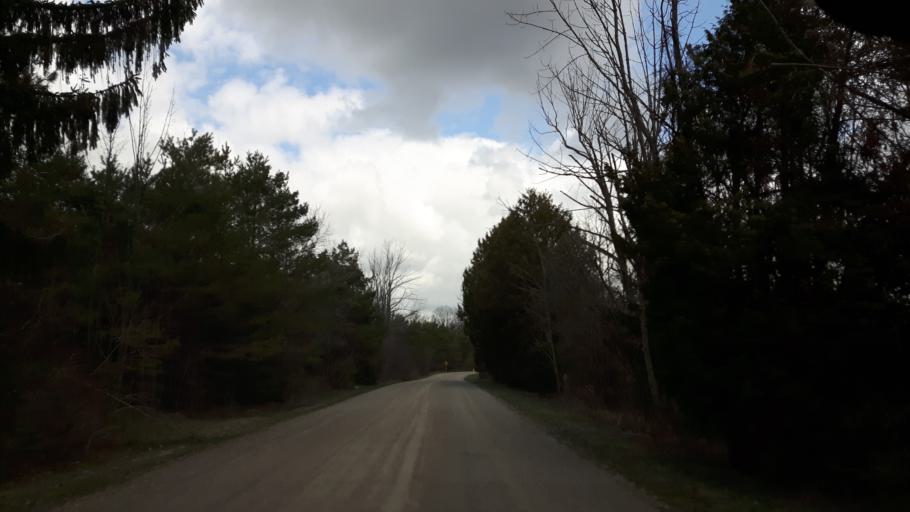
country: CA
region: Ontario
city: Bluewater
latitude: 43.5587
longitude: -81.6864
